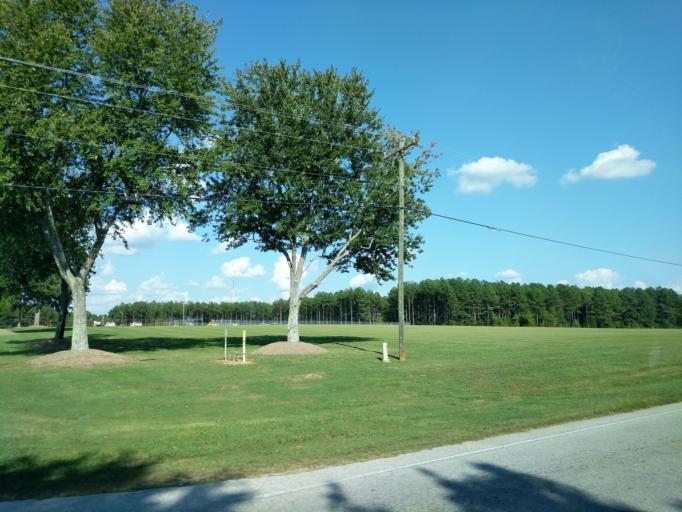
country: US
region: South Carolina
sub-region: Laurens County
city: Laurens
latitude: 34.5338
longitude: -82.0573
